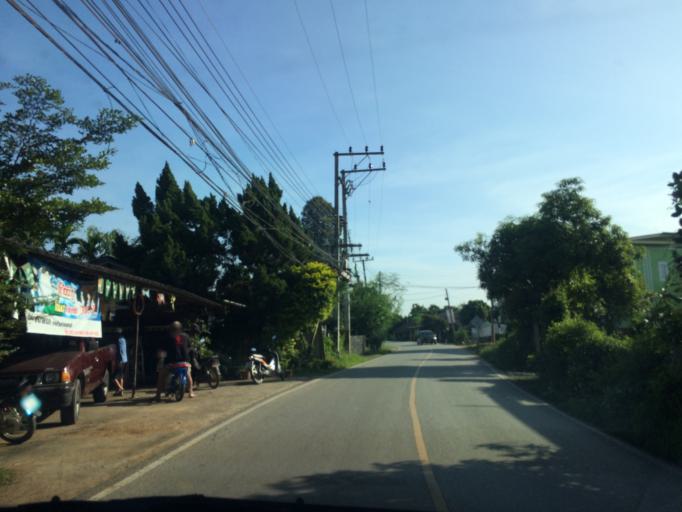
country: TH
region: Chiang Mai
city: Hang Dong
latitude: 18.6712
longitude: 98.9769
